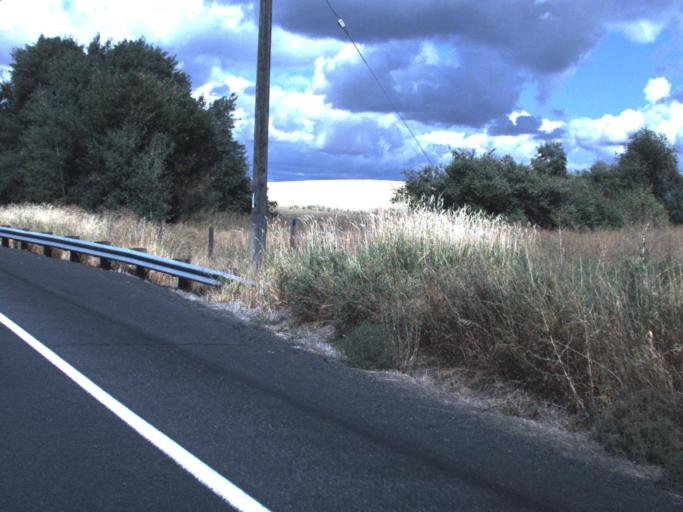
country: US
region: Washington
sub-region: Lincoln County
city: Davenport
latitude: 47.6100
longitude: -117.9372
